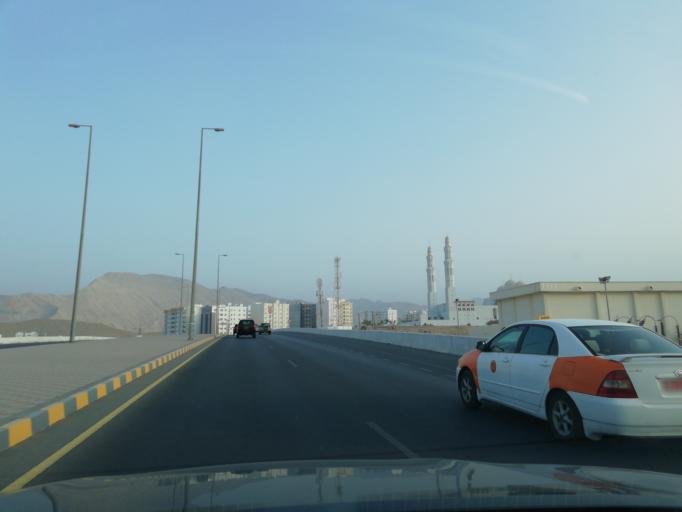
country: OM
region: Muhafazat Masqat
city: Bawshar
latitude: 23.5829
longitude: 58.4162
